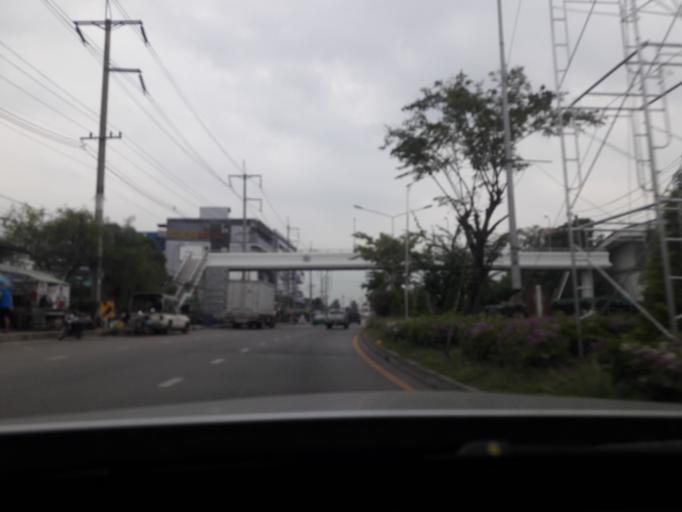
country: TH
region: Samut Songkhram
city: Samut Songkhram
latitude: 13.4129
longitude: 99.9995
